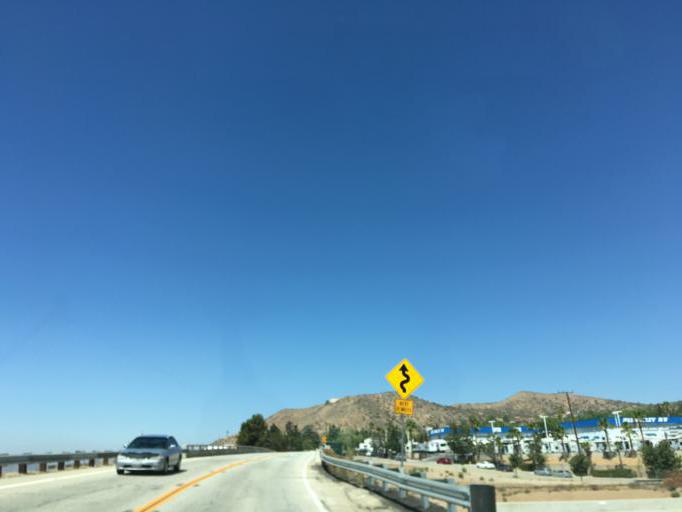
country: US
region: California
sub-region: Los Angeles County
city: Vincent
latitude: 34.4875
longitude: -118.1388
